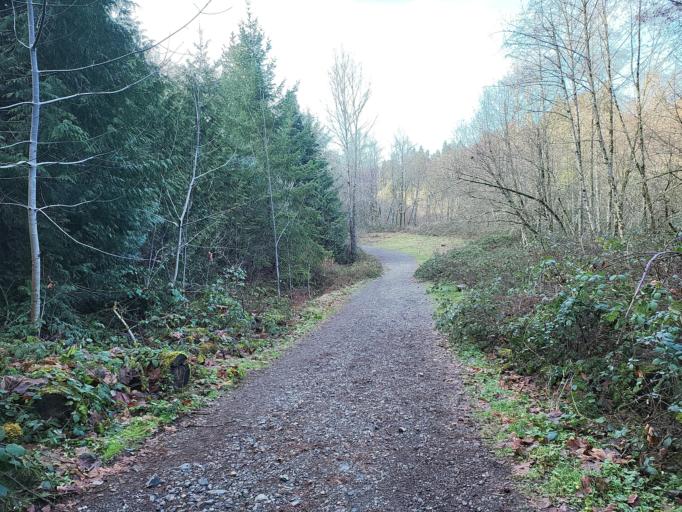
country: US
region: Washington
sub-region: King County
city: Newcastle
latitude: 47.5405
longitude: -122.1406
